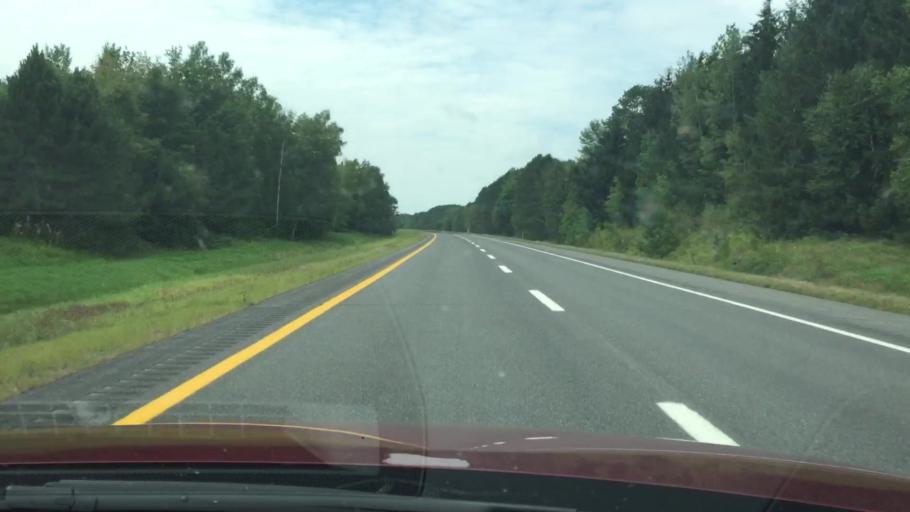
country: US
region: Maine
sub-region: Aroostook County
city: Houlton
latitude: 46.1404
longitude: -67.9282
